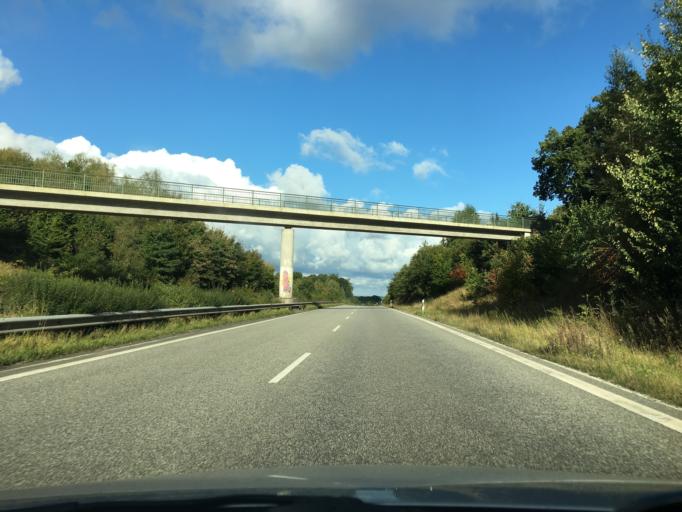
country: DE
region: Schleswig-Holstein
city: Heikendorf
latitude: 54.3498
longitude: 10.2097
